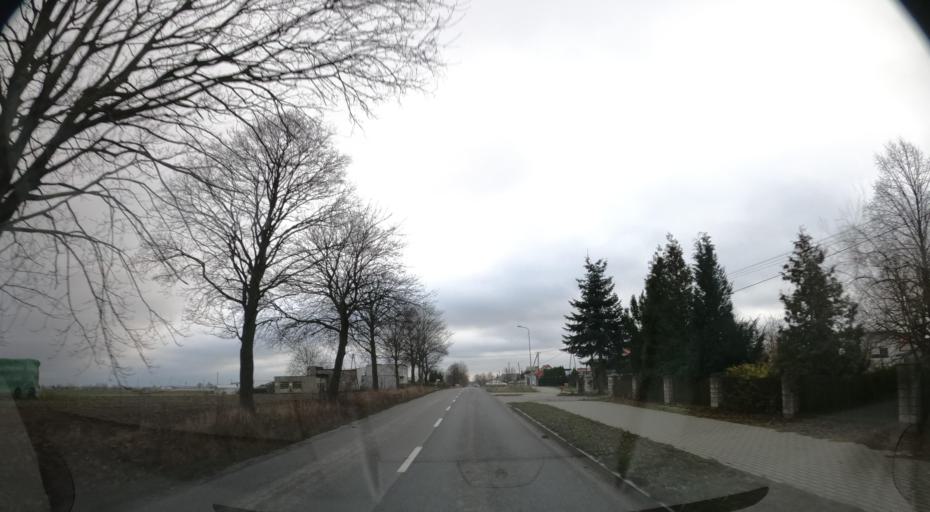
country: PL
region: Kujawsko-Pomorskie
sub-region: Powiat nakielski
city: Sadki
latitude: 53.1652
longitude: 17.4415
